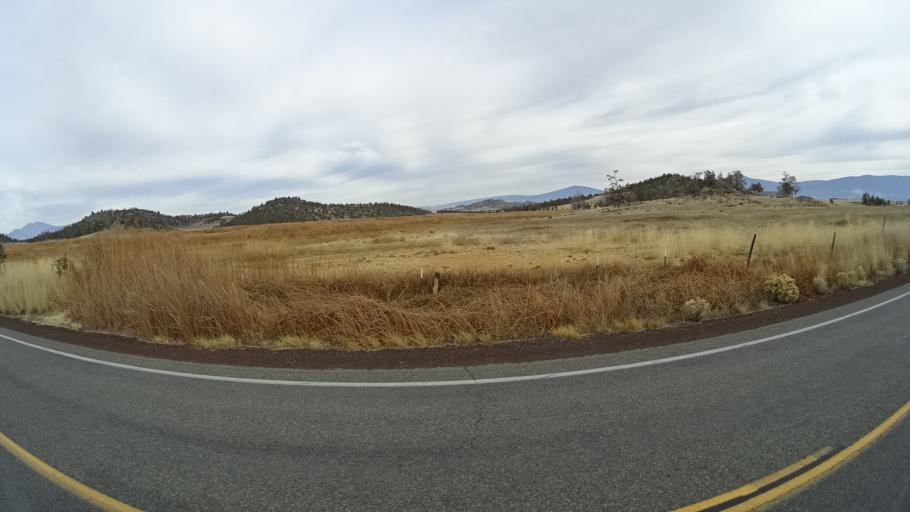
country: US
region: California
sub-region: Siskiyou County
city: Montague
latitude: 41.6426
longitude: -122.4864
